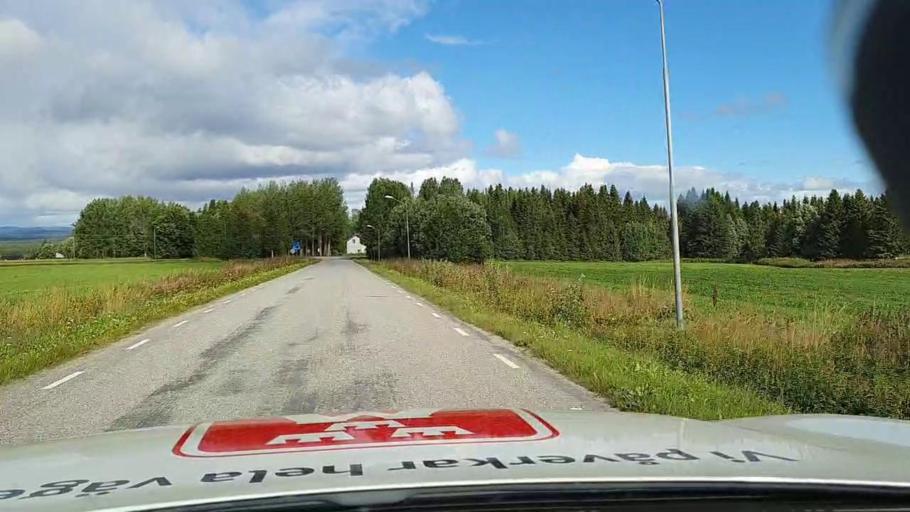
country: SE
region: Jaemtland
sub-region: Stroemsunds Kommun
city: Stroemsund
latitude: 63.8432
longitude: 15.3368
